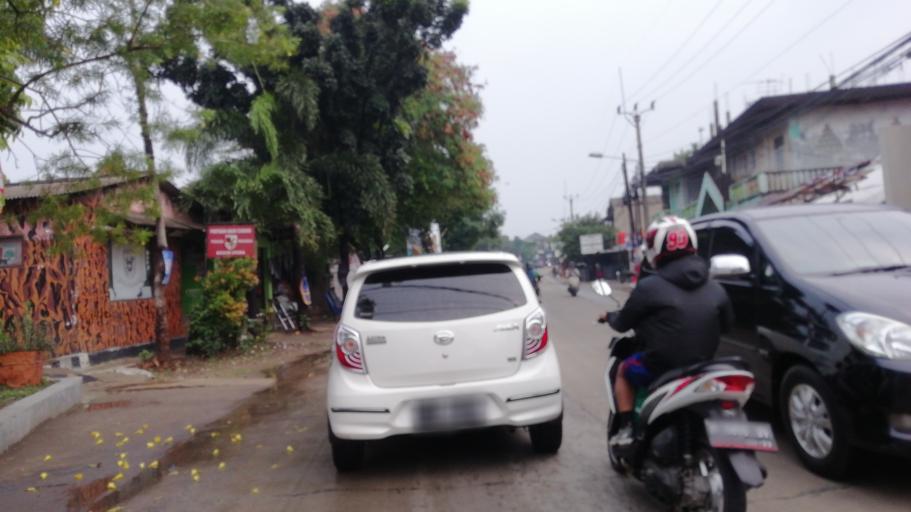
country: ID
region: West Java
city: Bogor
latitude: -6.5570
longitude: 106.8127
